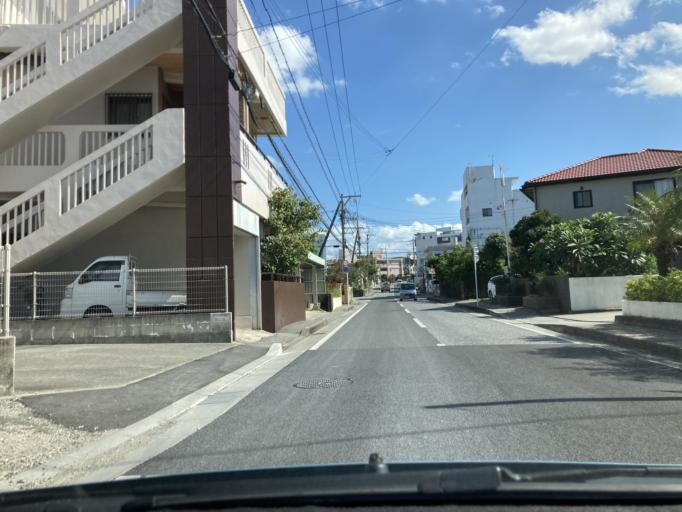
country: JP
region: Okinawa
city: Tomigusuku
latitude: 26.1875
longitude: 127.7136
